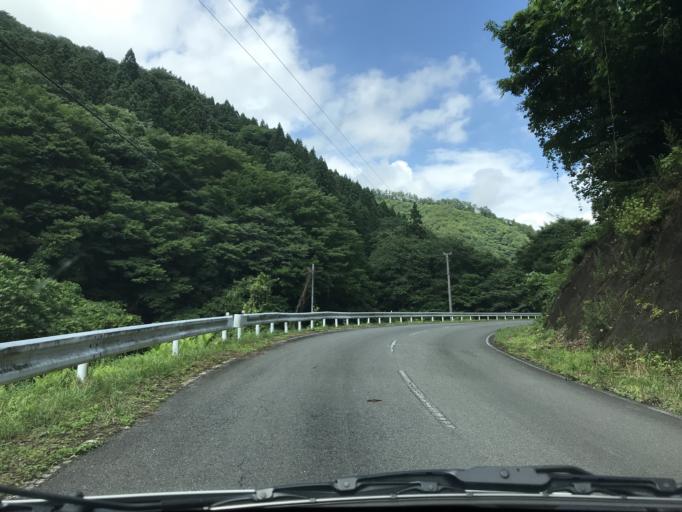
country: JP
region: Iwate
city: Tono
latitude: 39.0706
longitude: 141.4046
